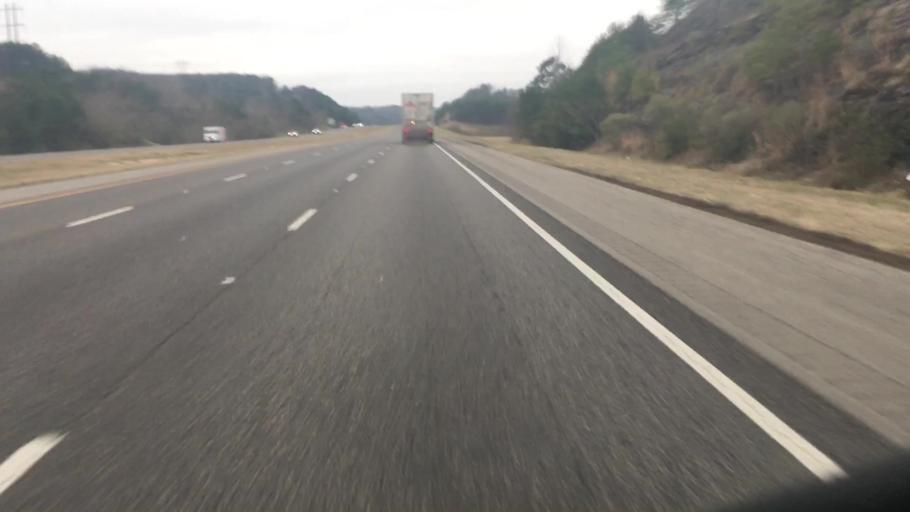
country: US
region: Alabama
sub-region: Jefferson County
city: Forestdale
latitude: 33.5997
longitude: -86.9002
